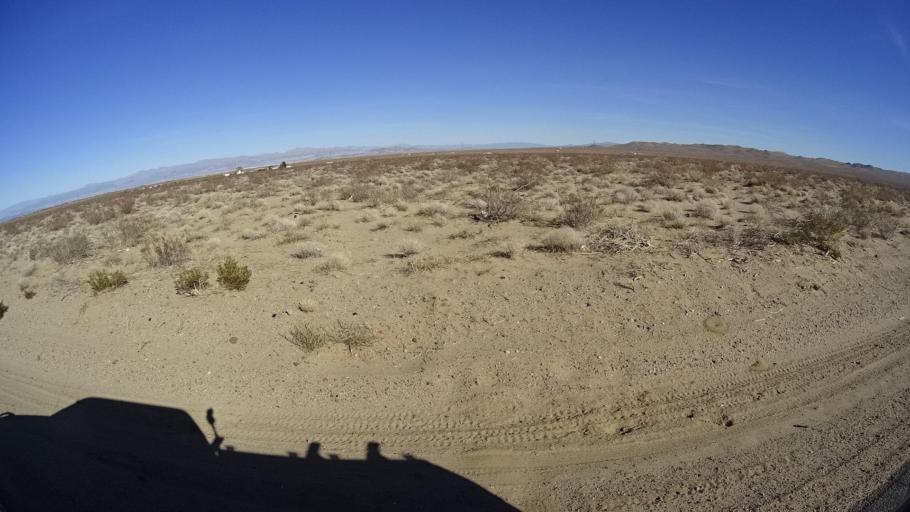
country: US
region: California
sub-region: Kern County
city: China Lake Acres
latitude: 35.5687
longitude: -117.7798
